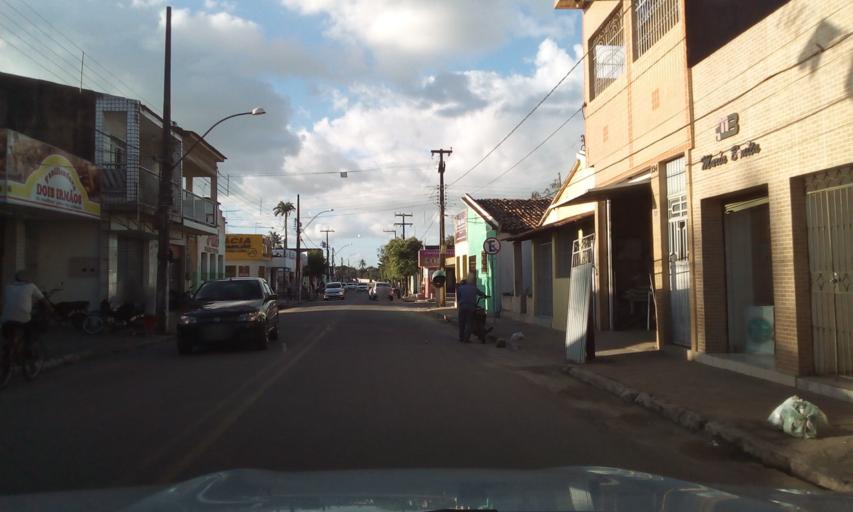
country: BR
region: Paraiba
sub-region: Mari
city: Mari
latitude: -7.0916
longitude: -35.2336
